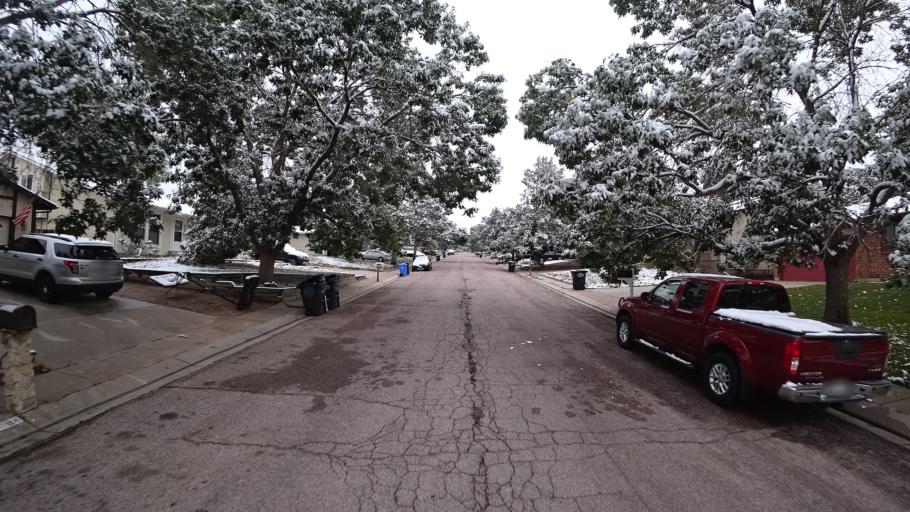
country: US
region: Colorado
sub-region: El Paso County
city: Cimarron Hills
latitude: 38.9248
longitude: -104.7713
